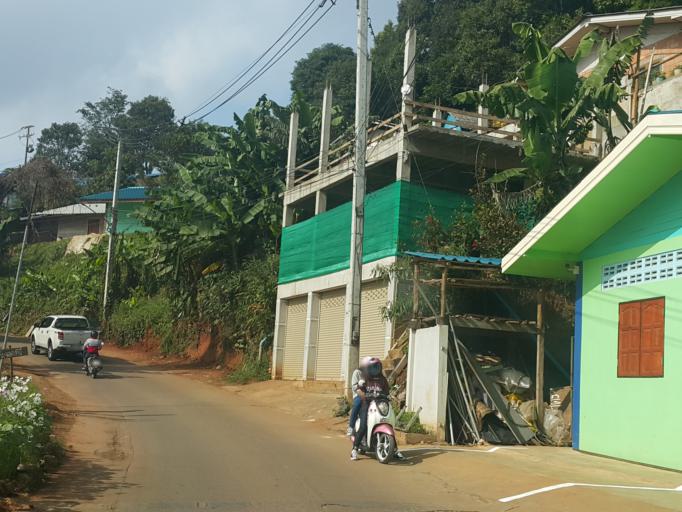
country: TH
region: Chiang Mai
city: Samoeng
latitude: 18.9343
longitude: 98.8237
